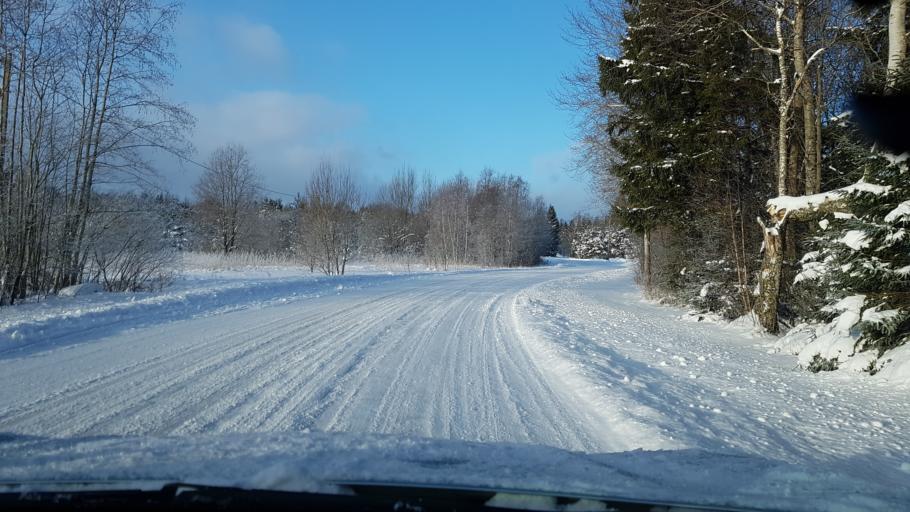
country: EE
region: Harju
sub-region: Nissi vald
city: Turba
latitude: 59.1116
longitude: 24.2238
